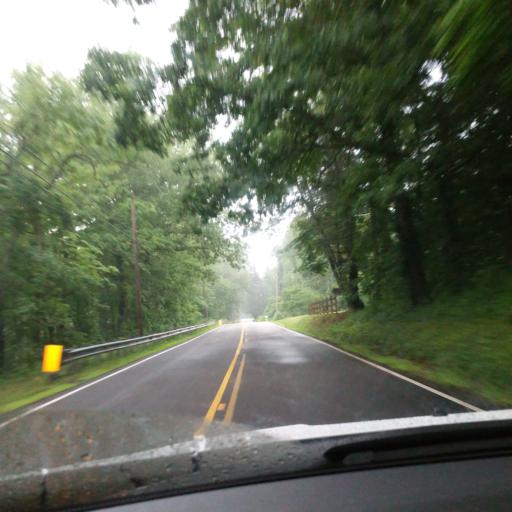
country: US
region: North Carolina
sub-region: Yancey County
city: Burnsville
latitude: 35.8247
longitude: -82.1893
